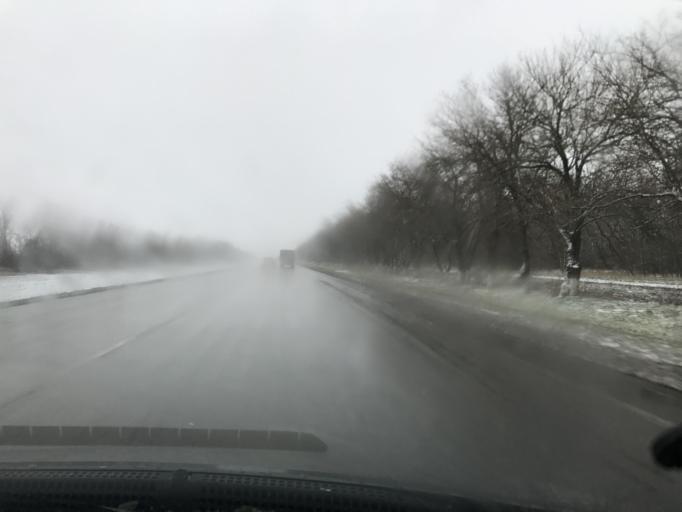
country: RU
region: Rostov
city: Yegorlykskaya
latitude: 46.6202
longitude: 40.5978
